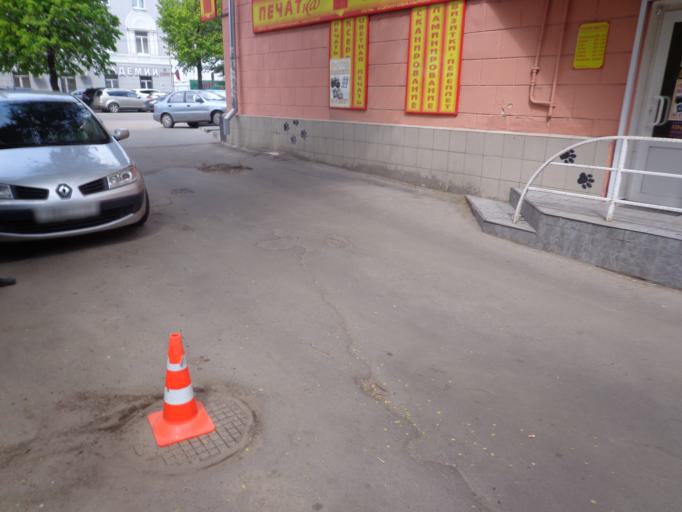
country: RU
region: Voronezj
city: Voronezh
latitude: 51.6767
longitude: 39.2133
